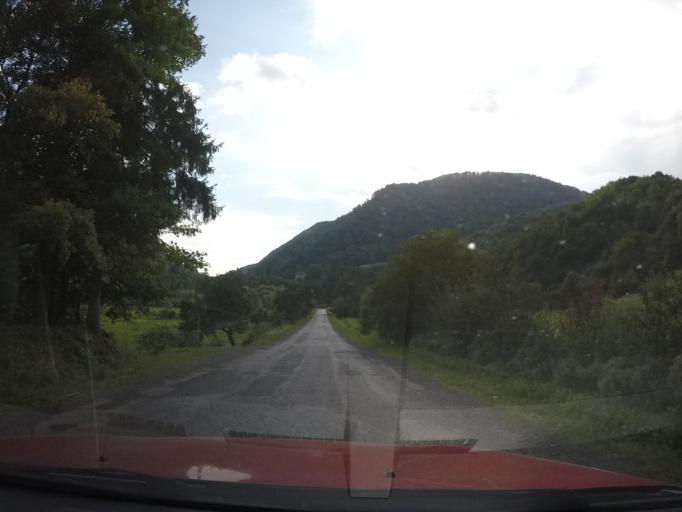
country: UA
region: Zakarpattia
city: Velykyi Bereznyi
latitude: 48.9516
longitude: 22.5106
